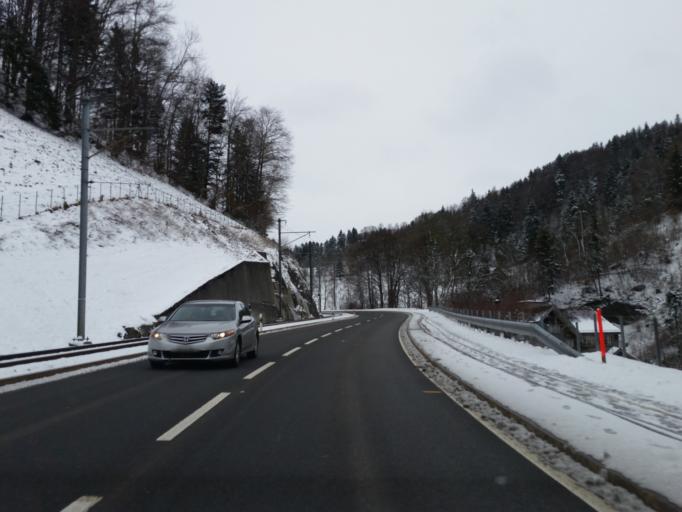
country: CH
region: Appenzell Ausserrhoden
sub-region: Bezirk Mittelland
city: Buhler
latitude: 47.3657
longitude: 9.4325
